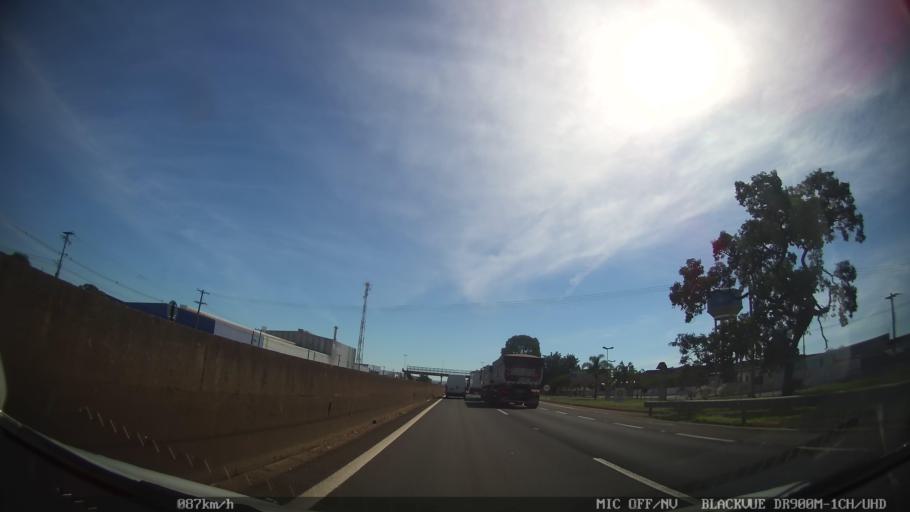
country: BR
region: Sao Paulo
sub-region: Porto Ferreira
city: Porto Ferreira
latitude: -21.8599
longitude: -47.4928
